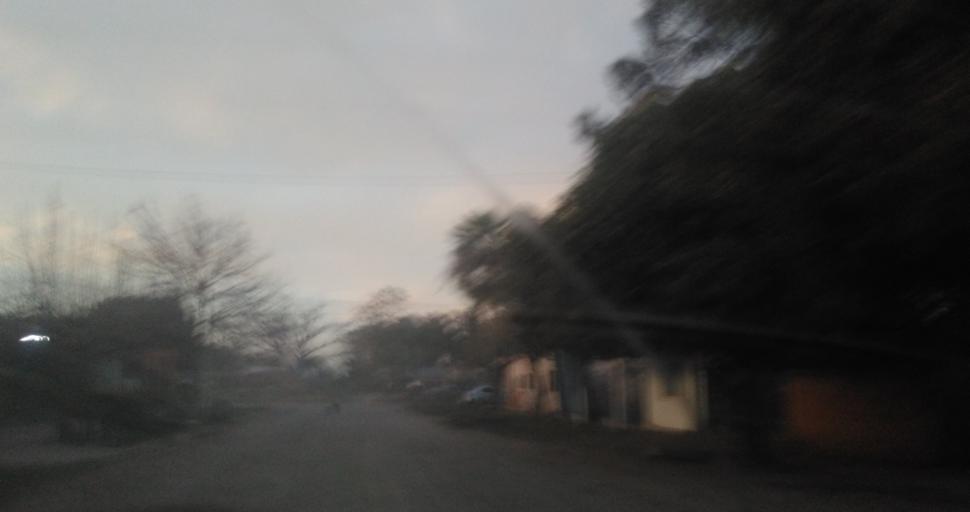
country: AR
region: Chaco
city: Fontana
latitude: -27.4334
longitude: -59.0167
